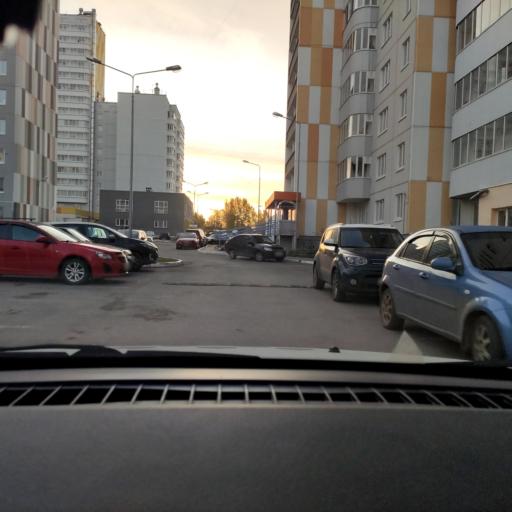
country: RU
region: Perm
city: Perm
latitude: 58.0518
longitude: 56.3493
